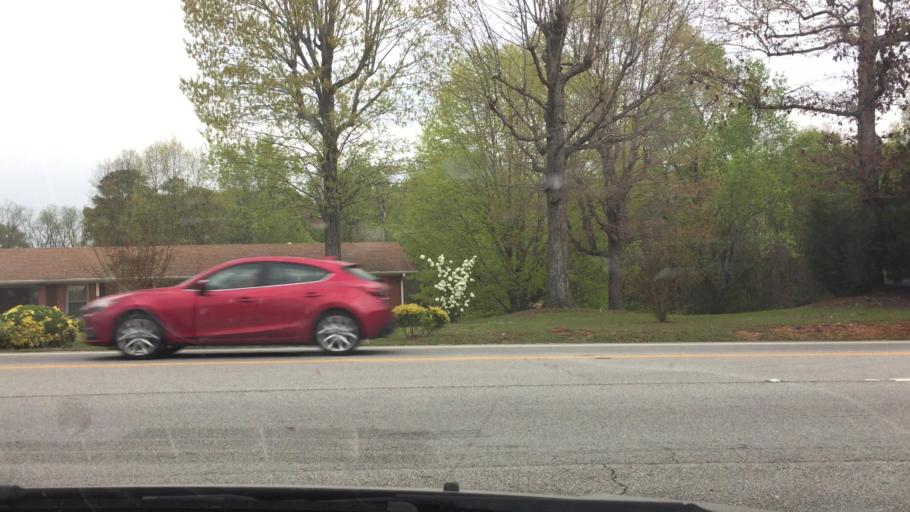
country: US
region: Georgia
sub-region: Henry County
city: Locust Grove
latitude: 33.3377
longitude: -84.0950
